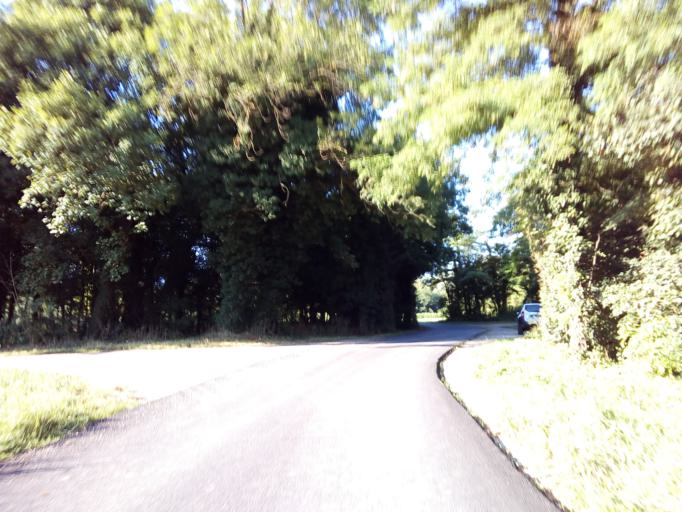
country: FR
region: Rhone-Alpes
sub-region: Departement de l'Isere
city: Saint-Vincent-de-Mercuze
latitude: 45.3640
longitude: 5.9676
